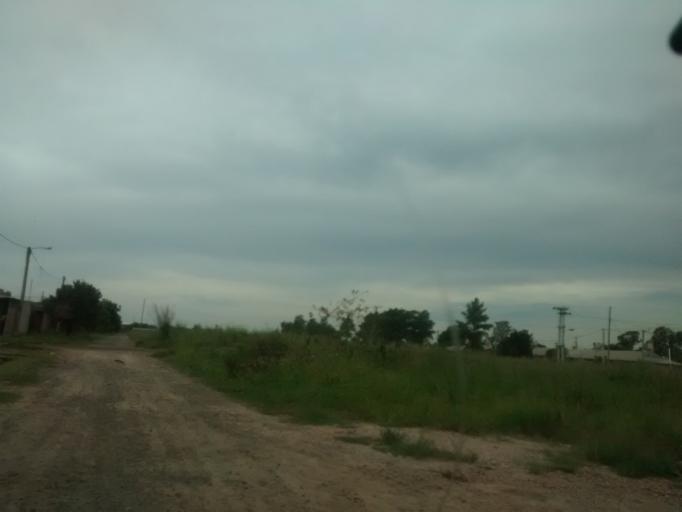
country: AR
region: Chaco
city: Fontana
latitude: -27.4585
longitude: -59.0347
